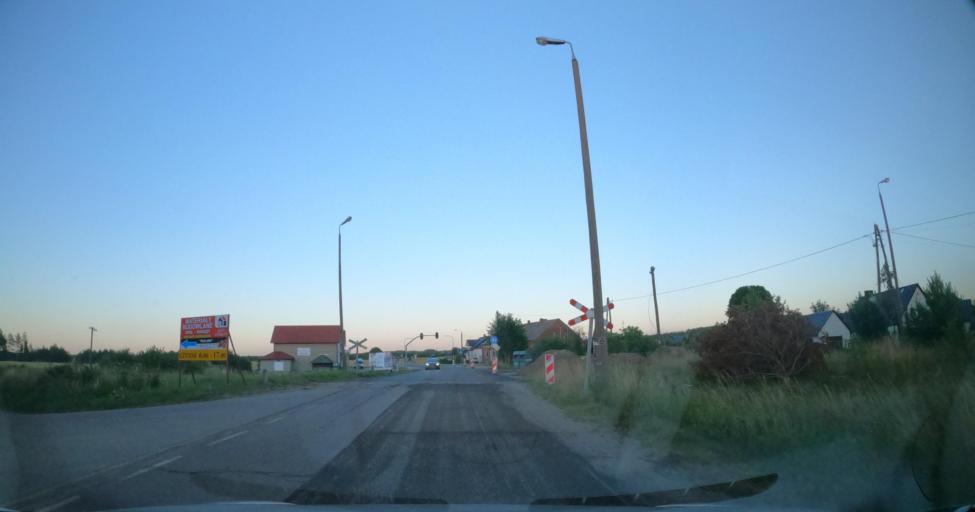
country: PL
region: Pomeranian Voivodeship
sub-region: Powiat wejherowski
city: Linia
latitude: 54.4548
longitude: 17.9114
